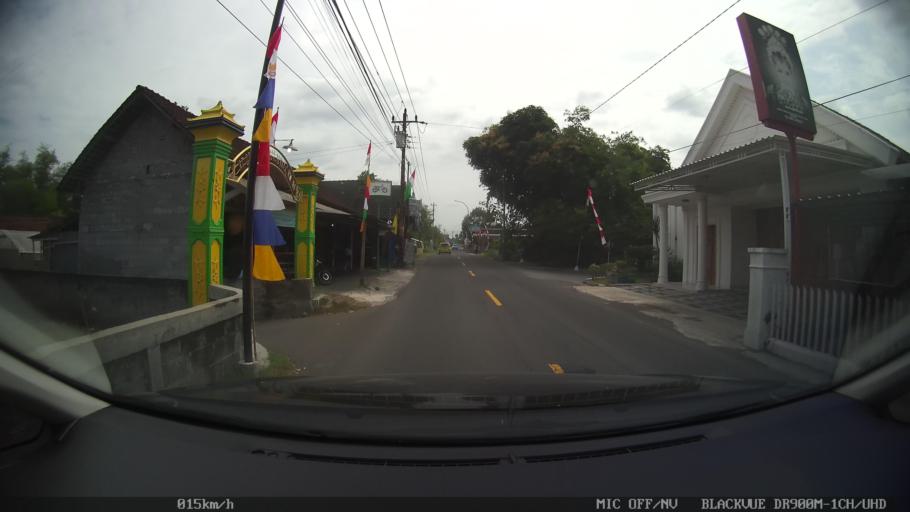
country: ID
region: Central Java
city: Candi Prambanan
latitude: -7.7364
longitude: 110.4808
